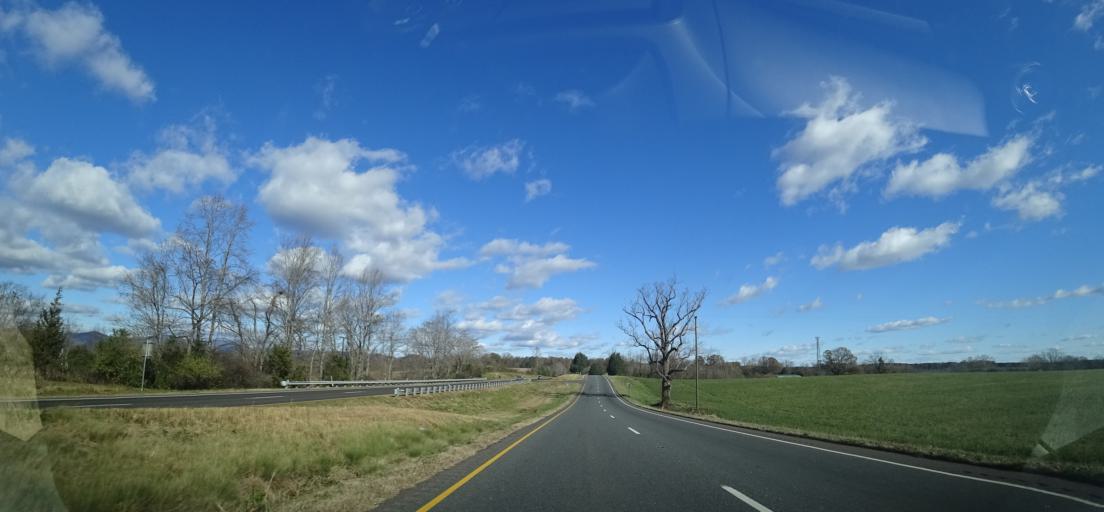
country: US
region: Virginia
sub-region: Greene County
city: Ruckersville
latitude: 38.3007
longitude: -78.3284
